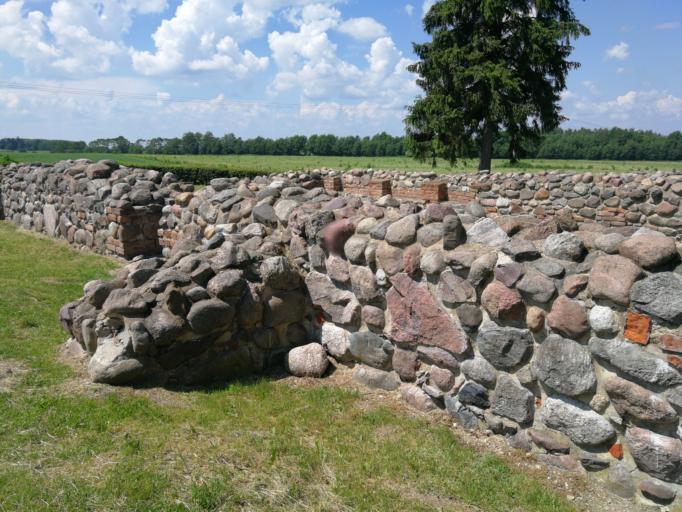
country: PL
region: Warmian-Masurian Voivodeship
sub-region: Powiat ostrodzki
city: Gierzwald
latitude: 53.4835
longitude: 20.1174
